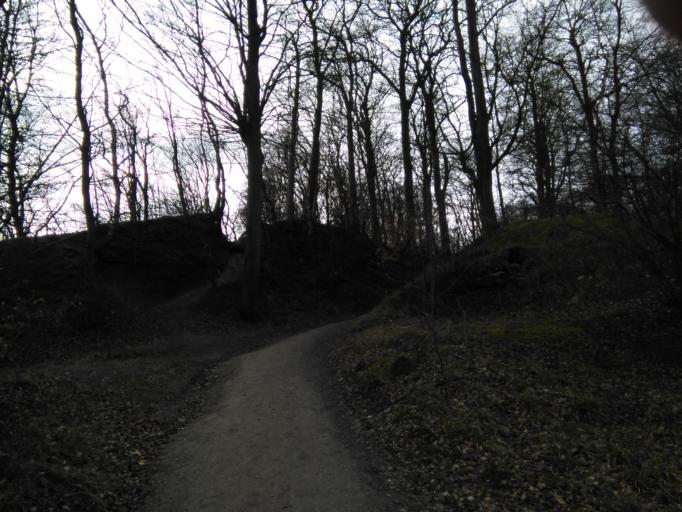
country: DK
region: Central Jutland
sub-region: Arhus Kommune
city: Arhus
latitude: 56.1242
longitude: 10.2183
